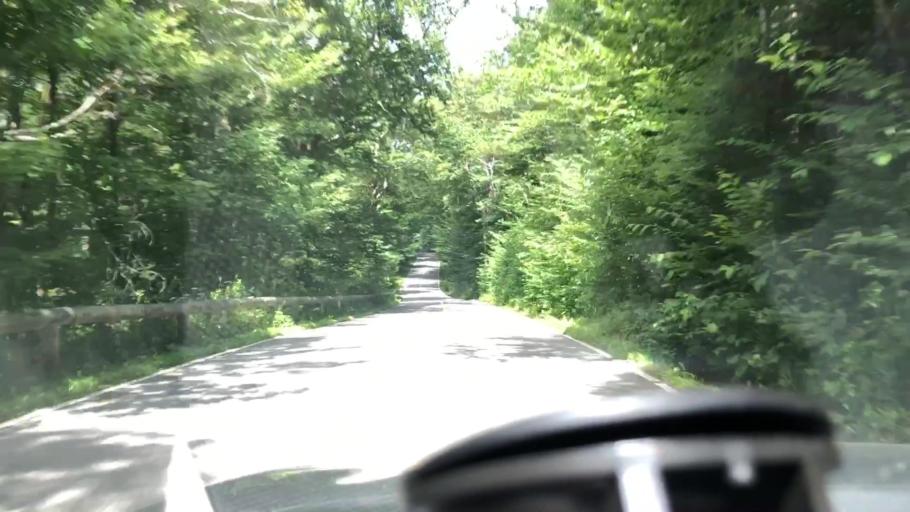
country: US
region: Massachusetts
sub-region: Berkshire County
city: Williamstown
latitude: 42.6661
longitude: -73.1666
